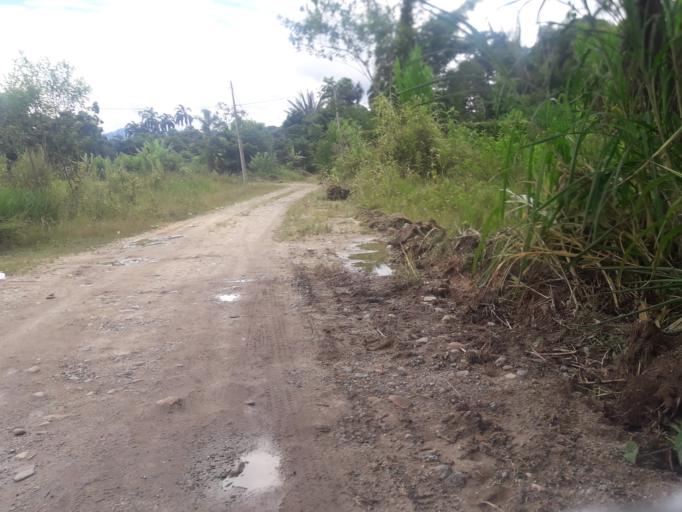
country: EC
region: Napo
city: Tena
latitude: -0.9794
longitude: -77.8510
